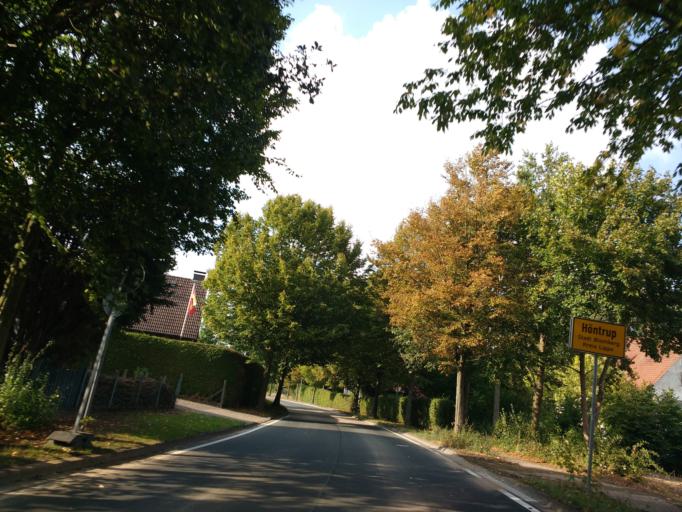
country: DE
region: North Rhine-Westphalia
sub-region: Regierungsbezirk Detmold
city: Bad Meinberg
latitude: 51.9255
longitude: 9.0320
